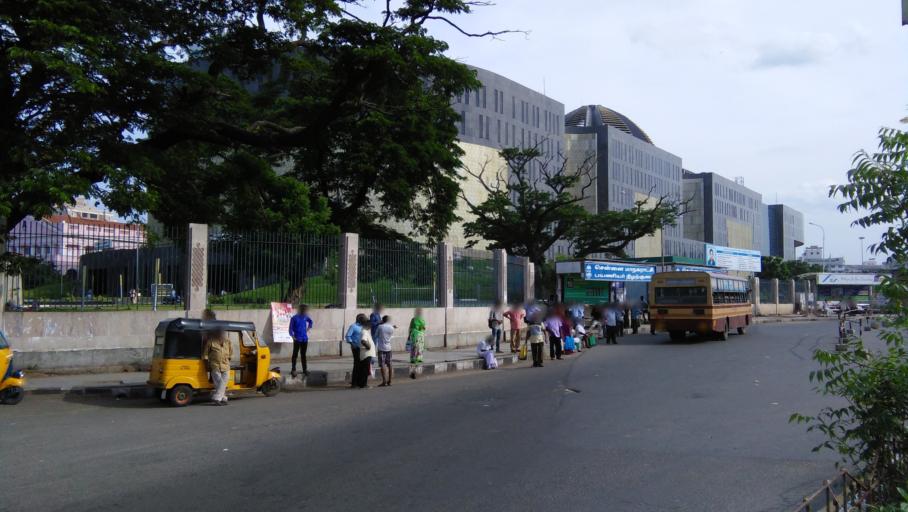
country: IN
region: Tamil Nadu
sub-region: Chennai
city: Chennai
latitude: 13.0710
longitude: 80.2744
